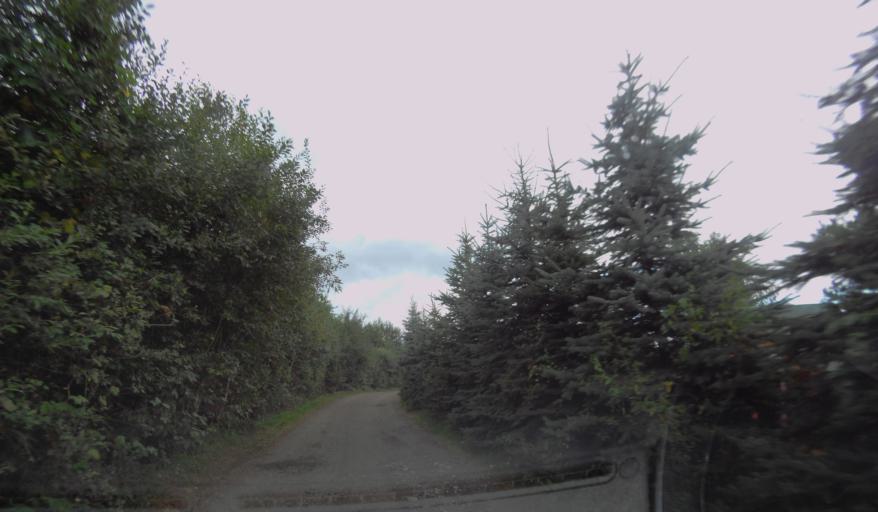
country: PL
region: Subcarpathian Voivodeship
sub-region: Powiat leski
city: Polanczyk
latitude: 49.3151
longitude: 22.5063
